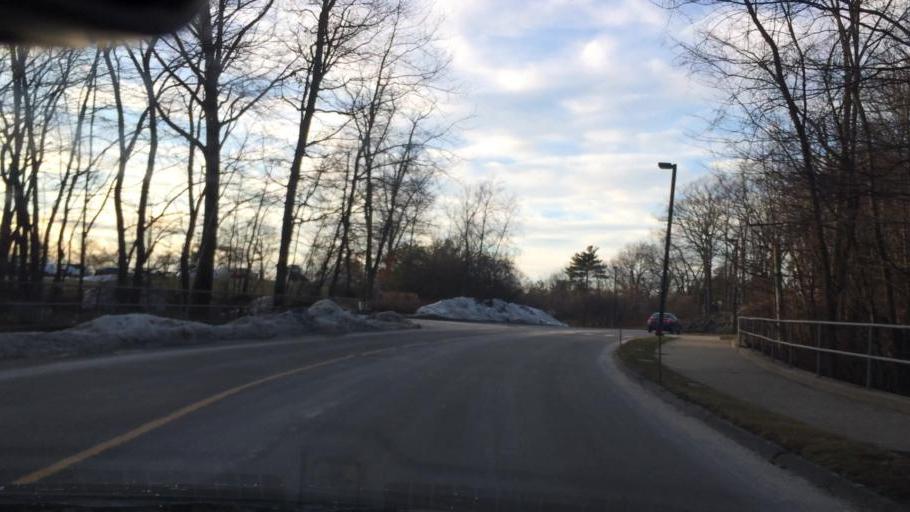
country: US
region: Massachusetts
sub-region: Middlesex County
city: Burlington
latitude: 42.4966
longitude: -71.1918
